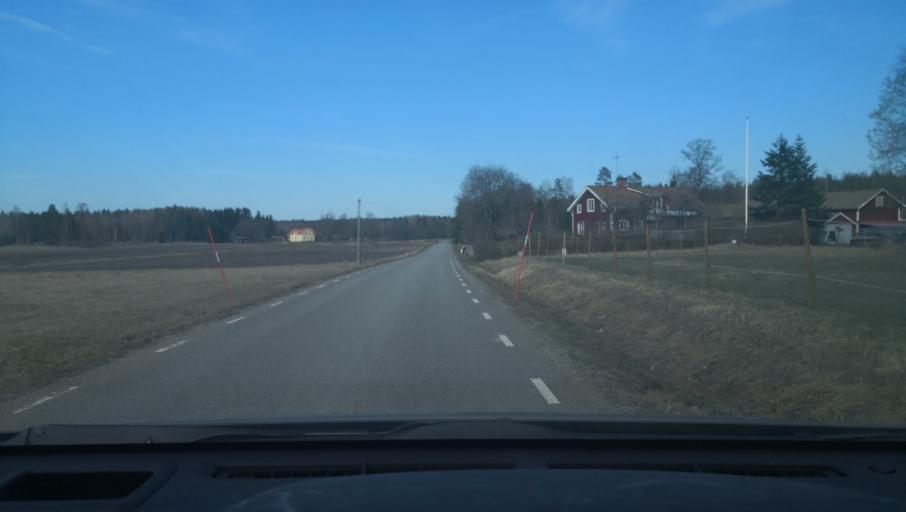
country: SE
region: Uppsala
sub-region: Heby Kommun
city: Heby
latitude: 59.8984
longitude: 16.8029
